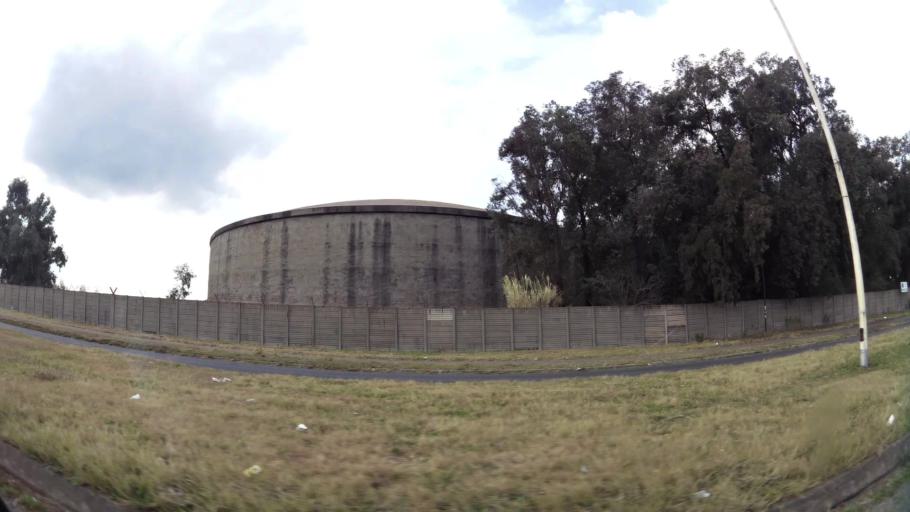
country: ZA
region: Gauteng
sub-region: Sedibeng District Municipality
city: Vanderbijlpark
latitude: -26.6861
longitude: 27.8225
